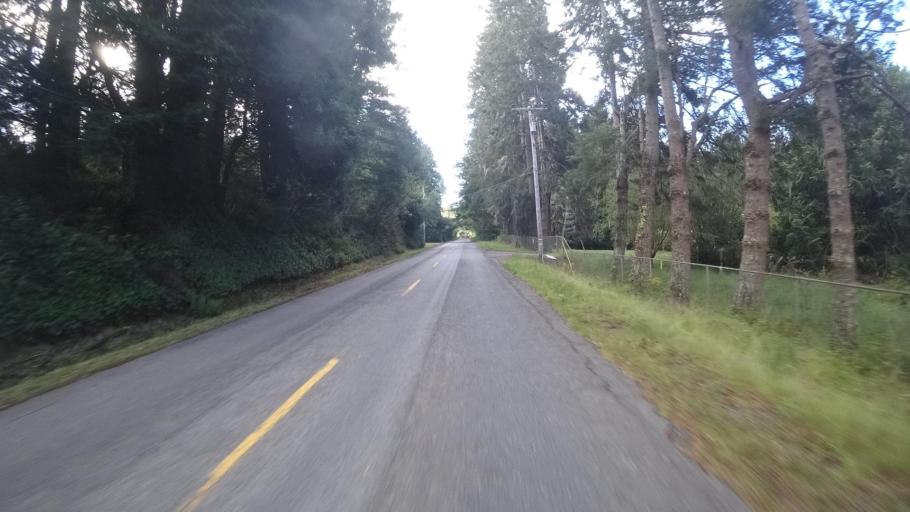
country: US
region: California
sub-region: Humboldt County
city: Westhaven-Moonstone
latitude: 41.0573
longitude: -124.1251
